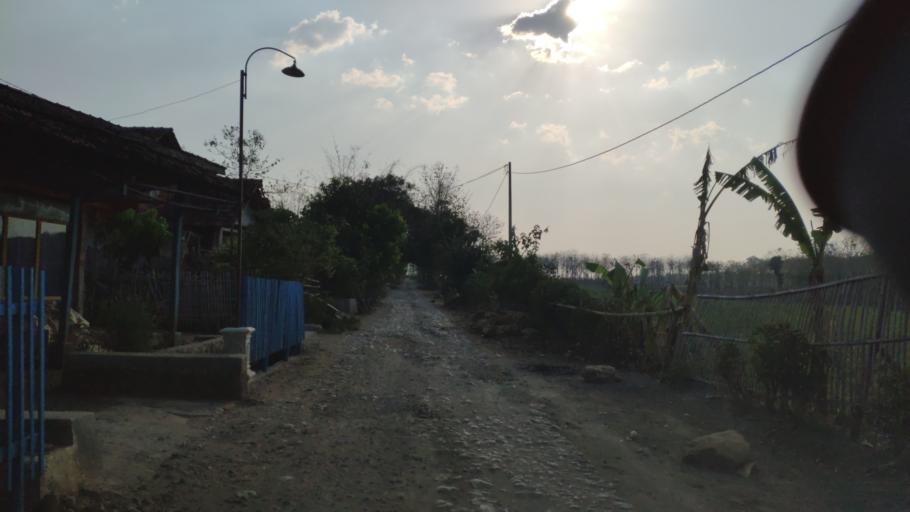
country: ID
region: Central Java
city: Pelem
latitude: -6.9944
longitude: 111.1941
